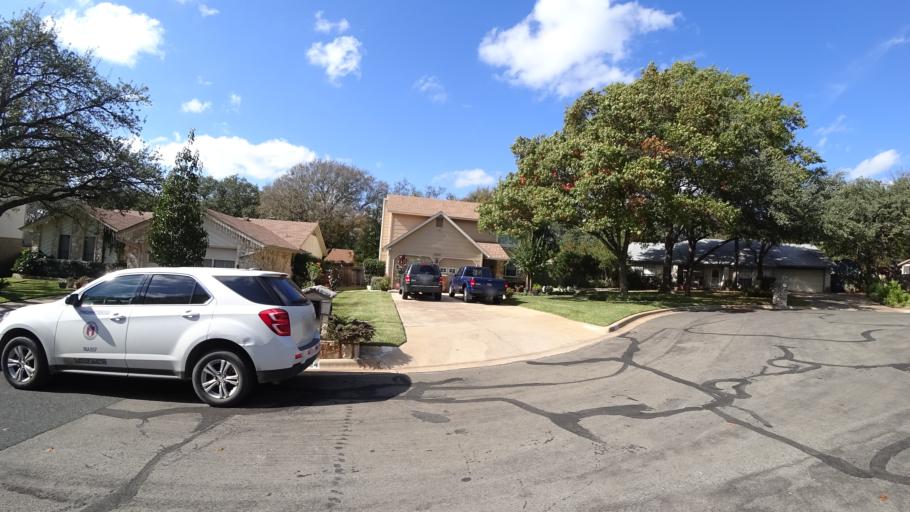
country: US
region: Texas
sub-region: Williamson County
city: Jollyville
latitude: 30.4169
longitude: -97.7266
